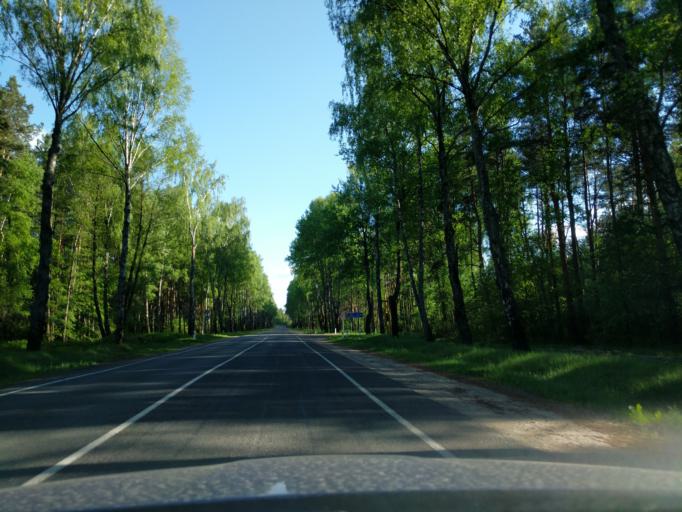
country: BY
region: Minsk
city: Myadzyel
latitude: 54.8511
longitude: 26.9253
